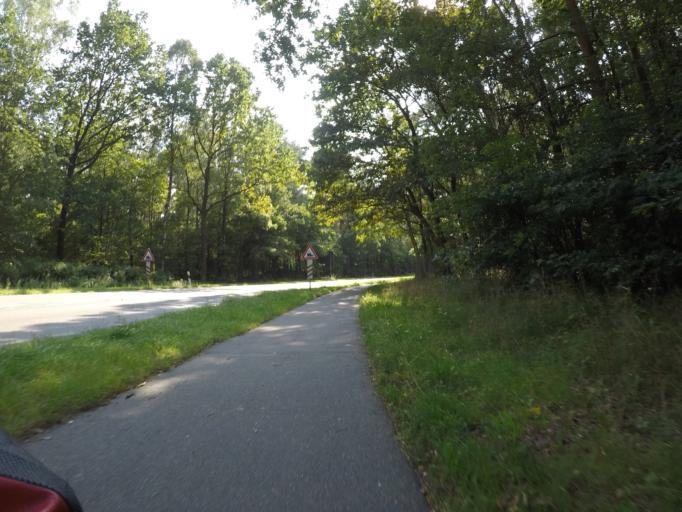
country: DE
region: Schleswig-Holstein
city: Wittenborn
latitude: 53.9485
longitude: 10.2233
